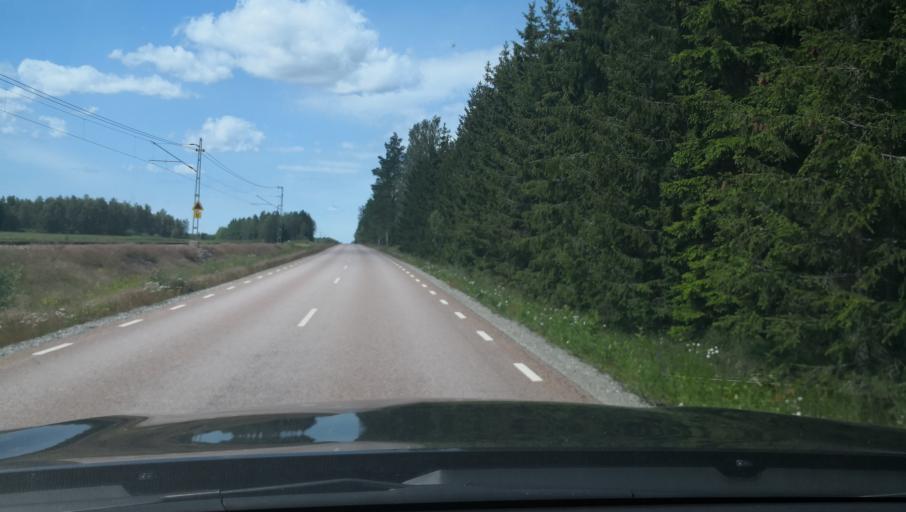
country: SE
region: Vaestmanland
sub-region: Surahammars Kommun
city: Ramnas
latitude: 59.8141
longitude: 16.1619
